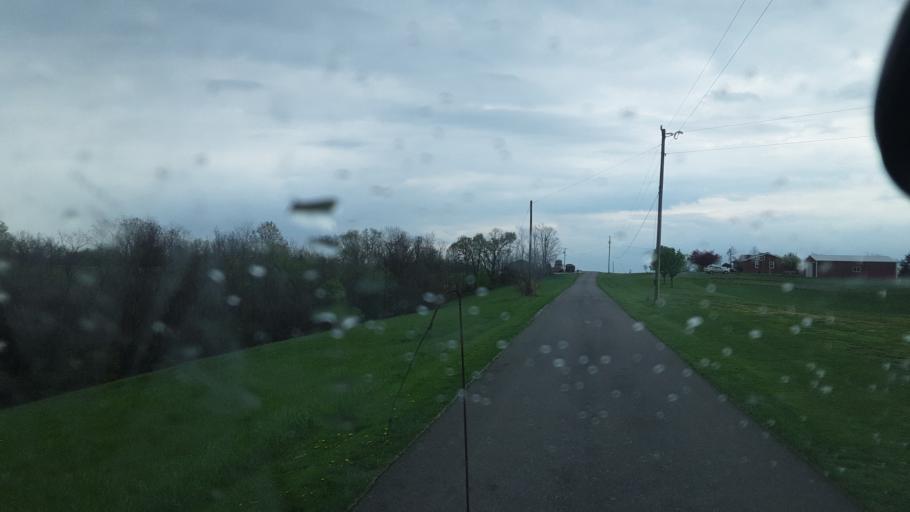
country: US
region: Kentucky
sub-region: Owen County
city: Owenton
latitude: 38.6740
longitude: -84.7873
